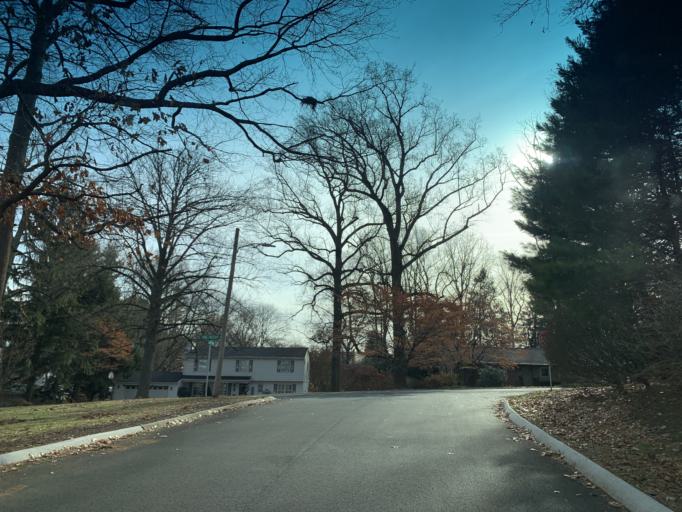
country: US
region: Maryland
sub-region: Harford County
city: South Bel Air
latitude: 39.5239
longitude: -76.3255
